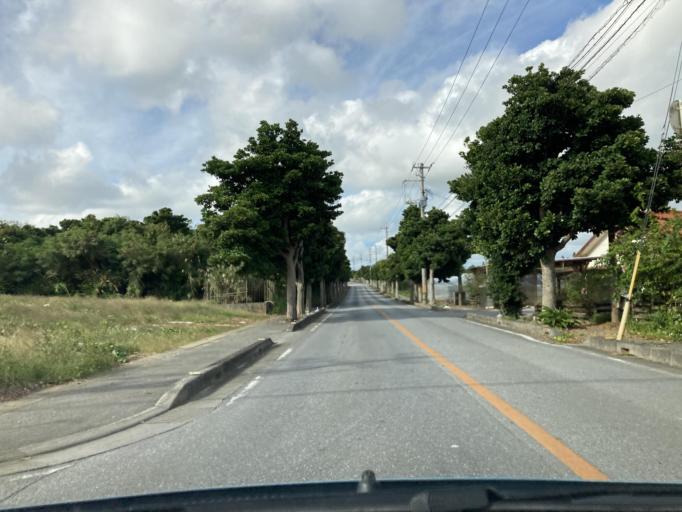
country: JP
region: Okinawa
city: Itoman
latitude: 26.1164
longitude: 127.7166
